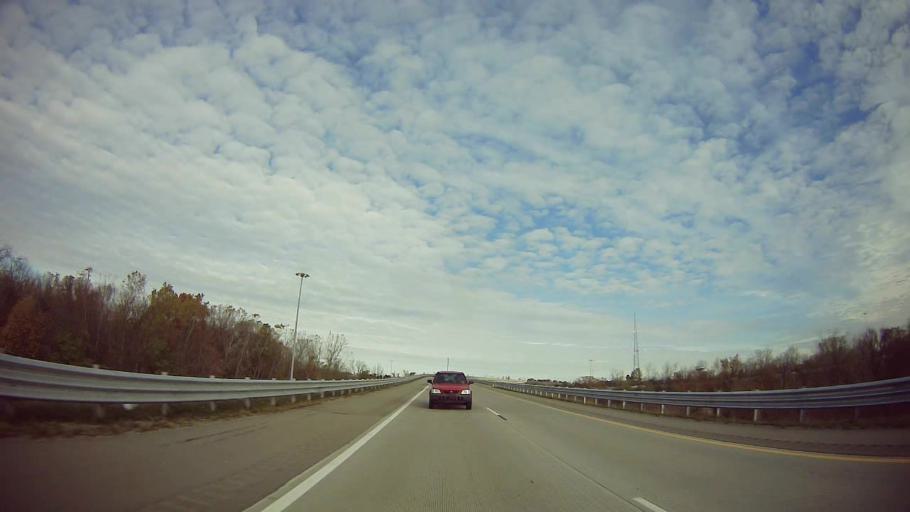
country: US
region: Michigan
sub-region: Oakland County
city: Novi
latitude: 42.4818
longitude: -83.4322
